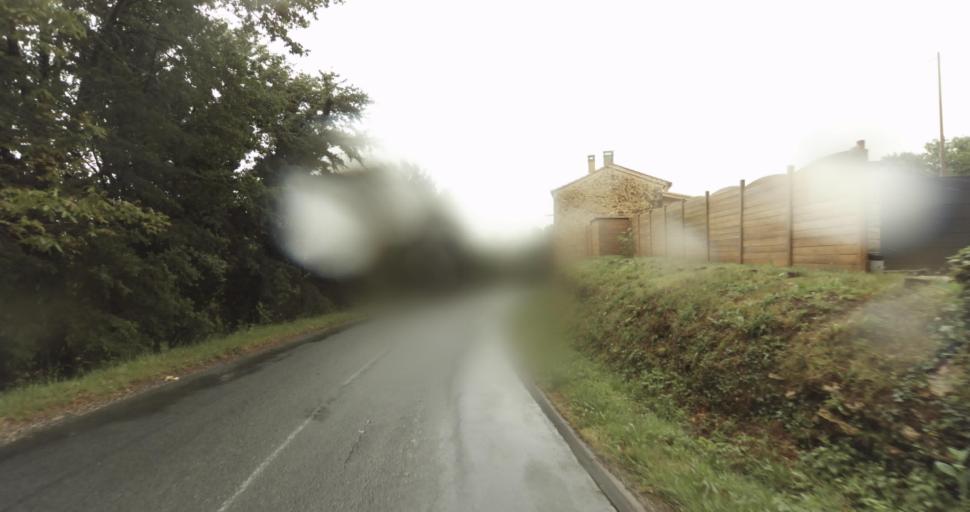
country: FR
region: Aquitaine
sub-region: Departement de la Dordogne
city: Le Bugue
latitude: 44.8281
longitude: 0.8931
